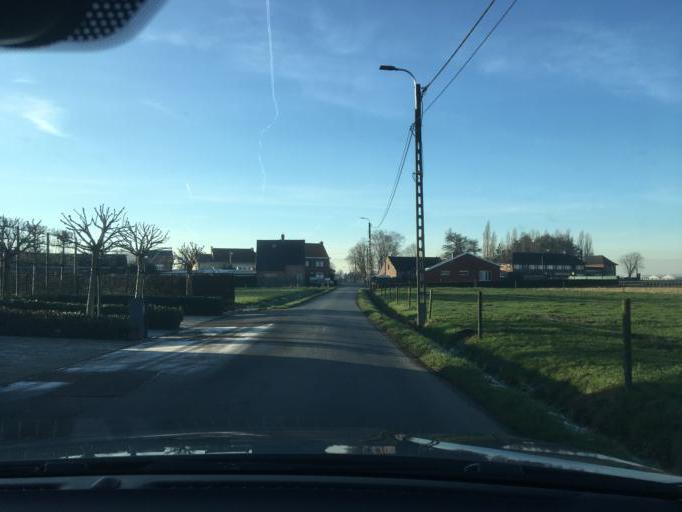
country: BE
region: Flanders
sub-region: Provincie West-Vlaanderen
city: Pittem
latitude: 50.9647
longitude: 3.2461
